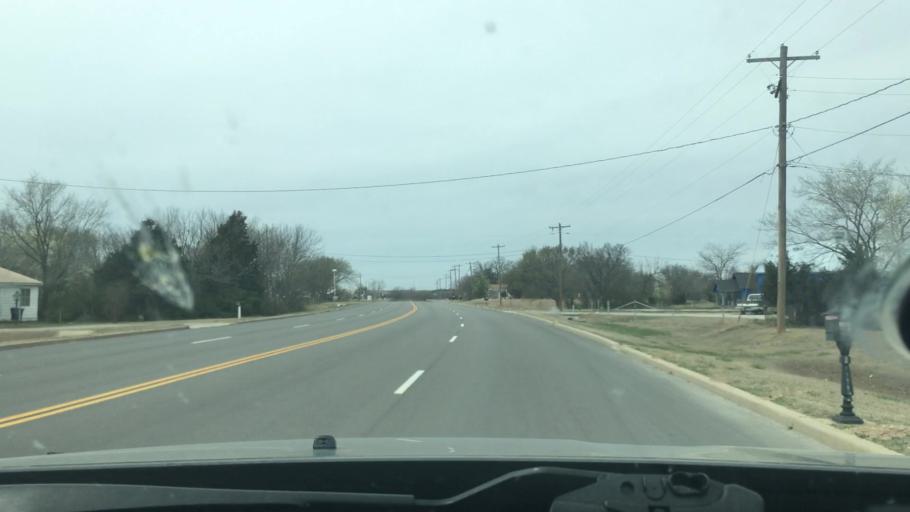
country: US
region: Oklahoma
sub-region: Seminole County
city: Seminole
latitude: 35.2579
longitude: -96.7100
